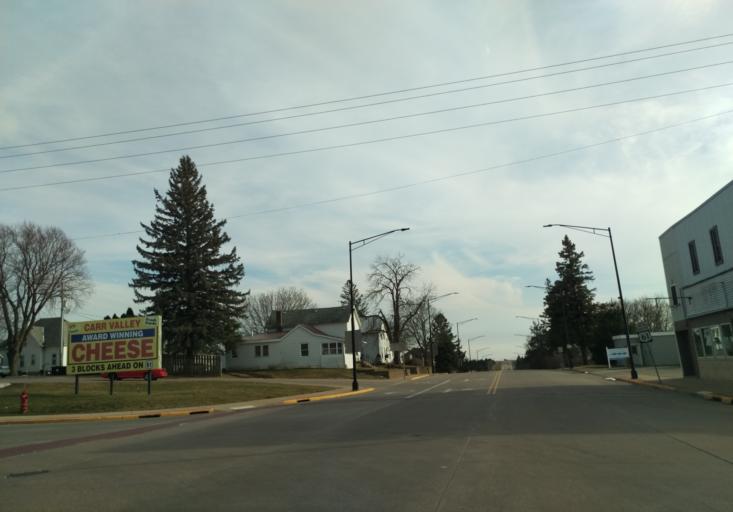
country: US
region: Wisconsin
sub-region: Grant County
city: Fennimore
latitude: 42.9812
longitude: -90.6556
